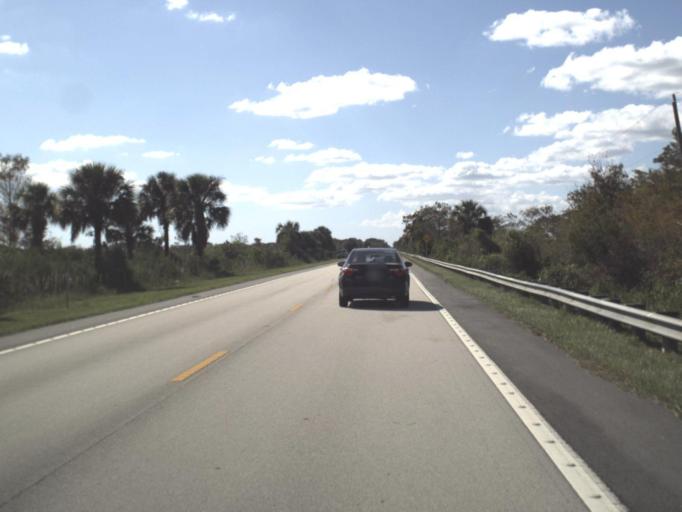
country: US
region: Florida
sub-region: Collier County
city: Marco
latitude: 25.8730
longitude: -81.1919
